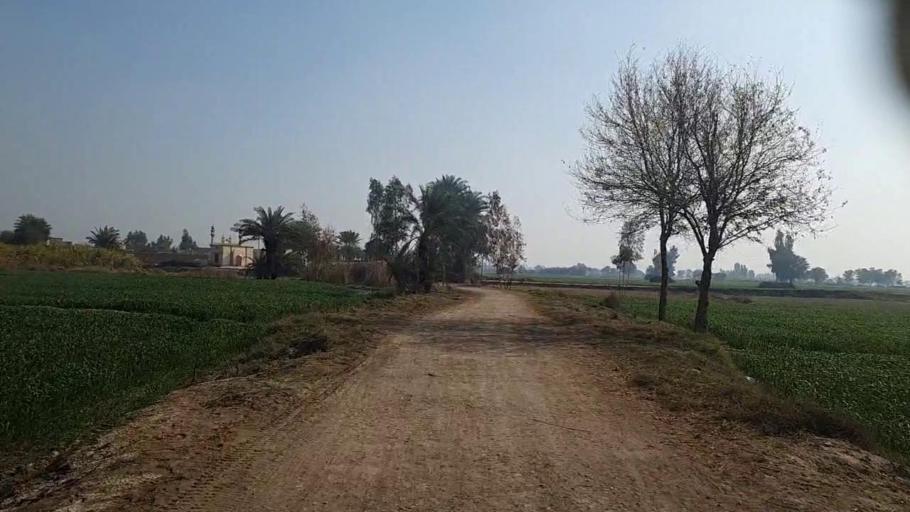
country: PK
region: Sindh
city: Khairpur
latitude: 27.9262
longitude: 69.6679
